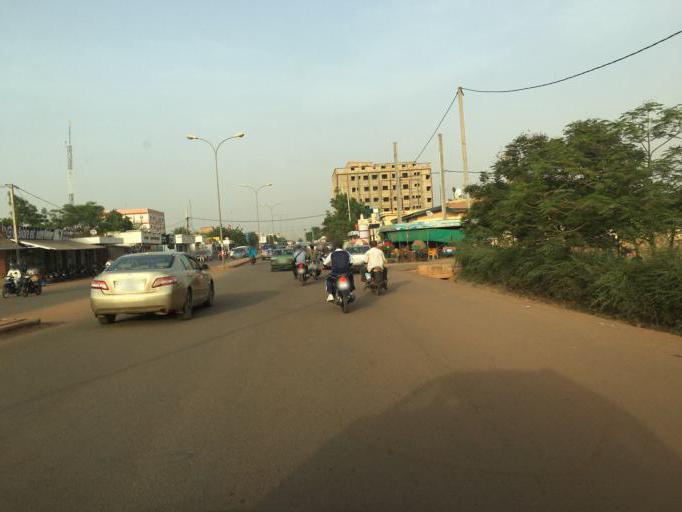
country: BF
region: Centre
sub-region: Kadiogo Province
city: Ouagadougou
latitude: 12.3687
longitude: -1.5003
